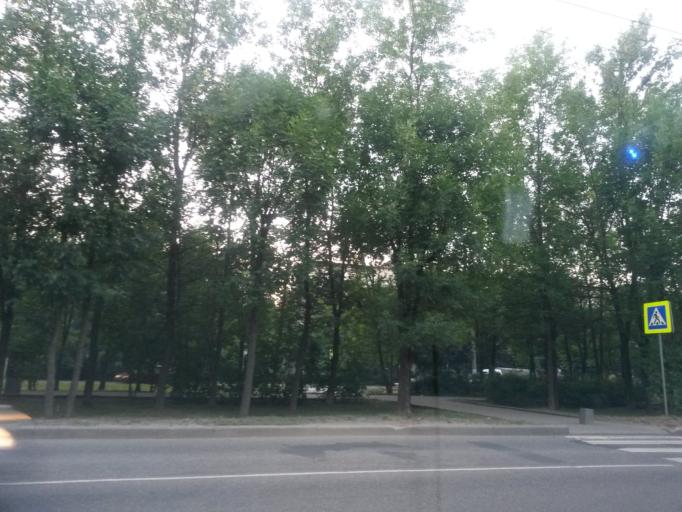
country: RU
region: Ivanovo
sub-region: Gorod Ivanovo
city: Ivanovo
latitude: 56.9611
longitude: 41.0122
